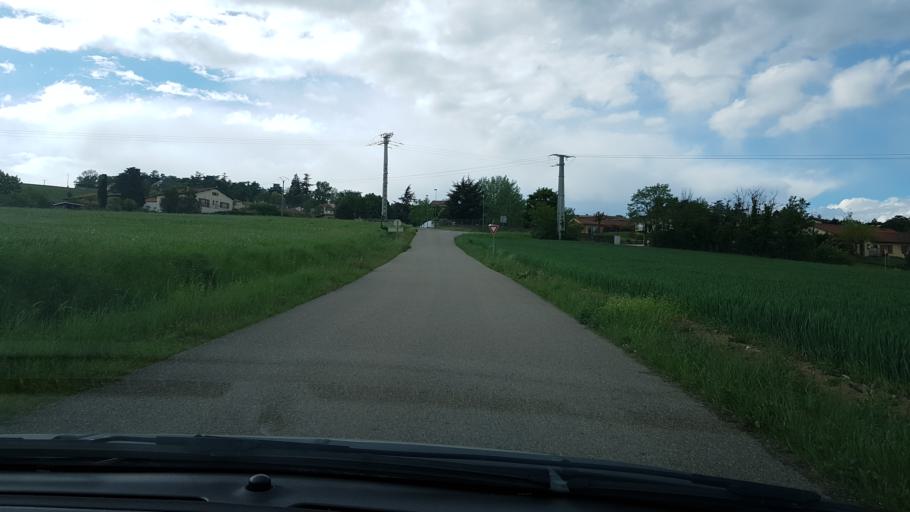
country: FR
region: Rhone-Alpes
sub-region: Departement du Rhone
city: Saint-Maurice-sur-Dargoire
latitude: 45.5792
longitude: 4.6357
